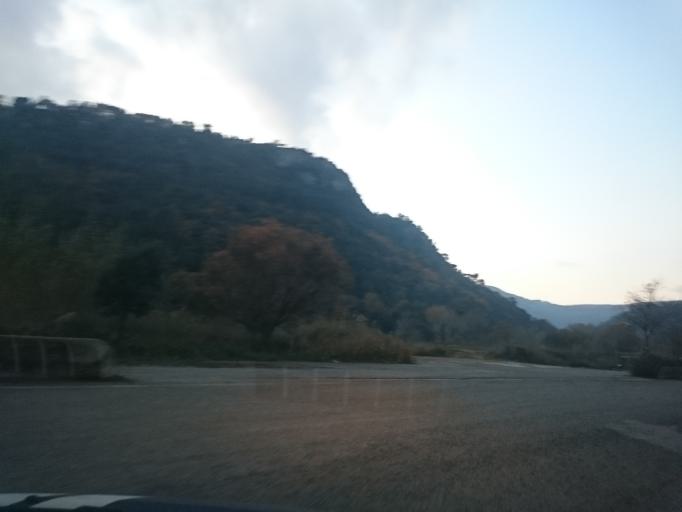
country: ES
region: Catalonia
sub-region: Provincia de Barcelona
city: Tagamanent
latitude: 41.7463
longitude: 2.2653
